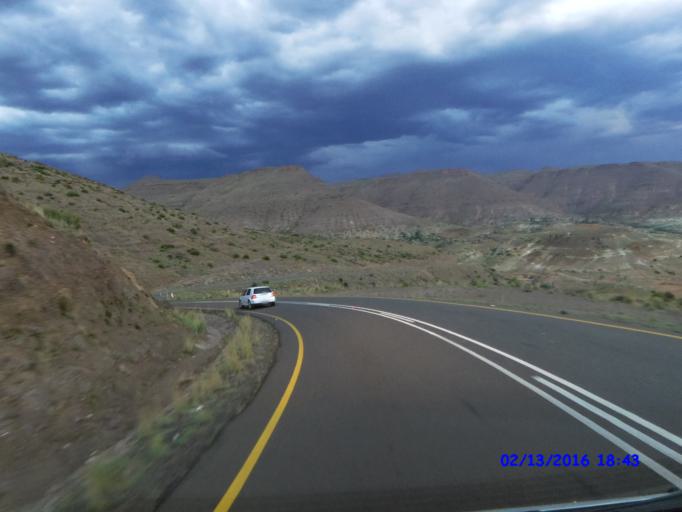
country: LS
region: Qacha's Nek
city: Qacha's Nek
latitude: -30.0469
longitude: 28.3075
